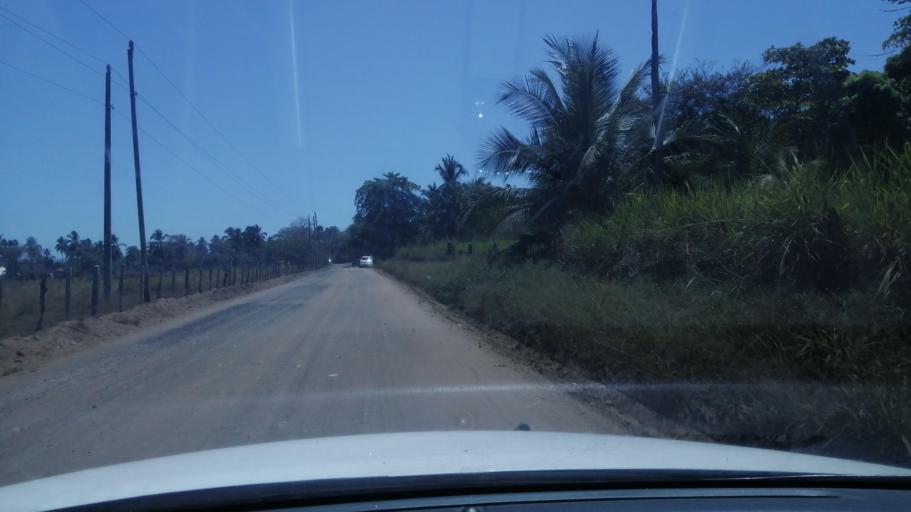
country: PA
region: Chiriqui
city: San Felix
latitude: 8.1703
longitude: -81.8676
